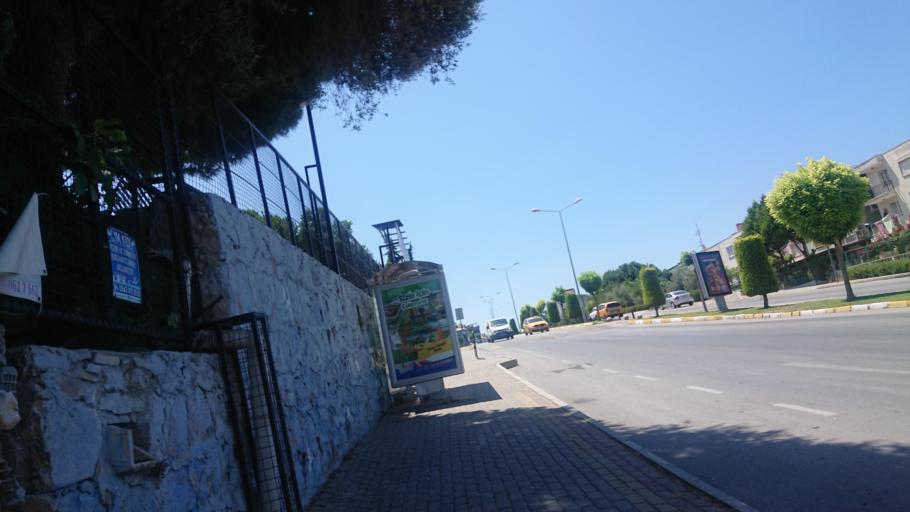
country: TR
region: Aydin
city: Kusadasi
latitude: 37.8677
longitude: 27.2683
